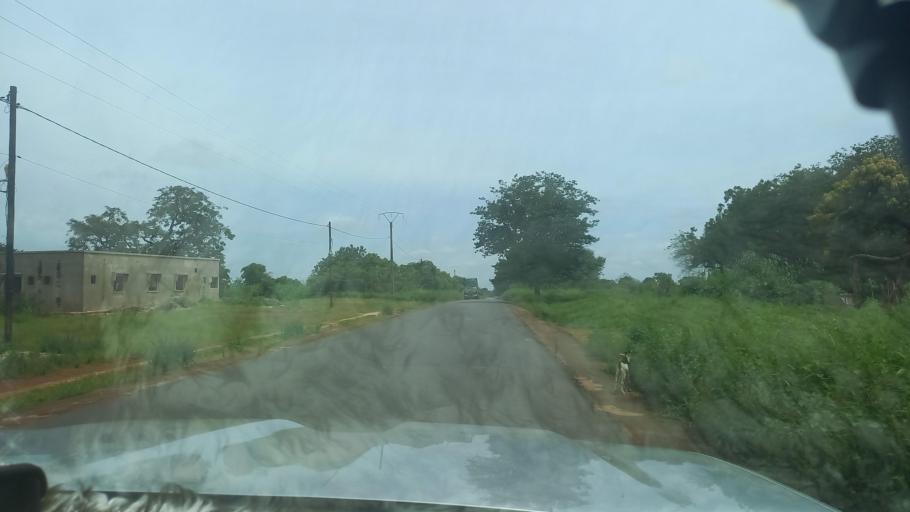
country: SN
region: Kolda
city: Marsassoum
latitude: 12.9623
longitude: -15.9833
